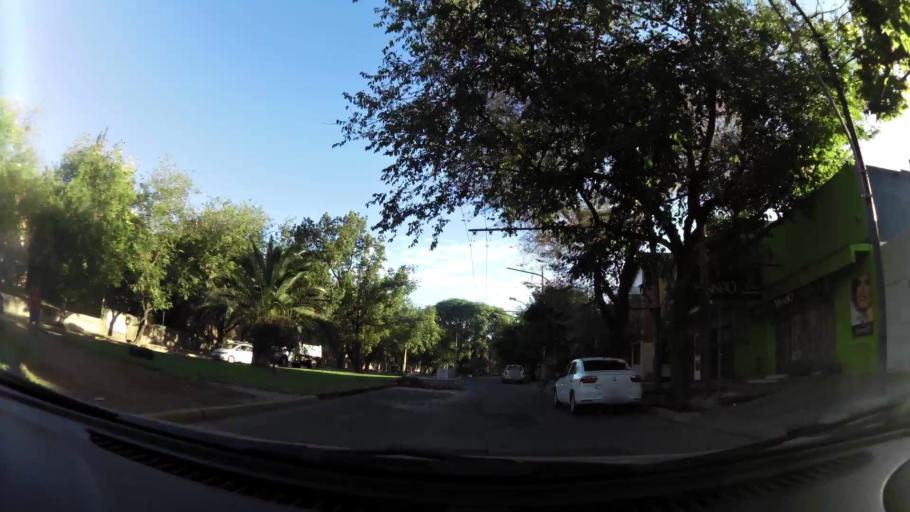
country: AR
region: Mendoza
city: Mendoza
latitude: -32.8733
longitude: -68.8398
